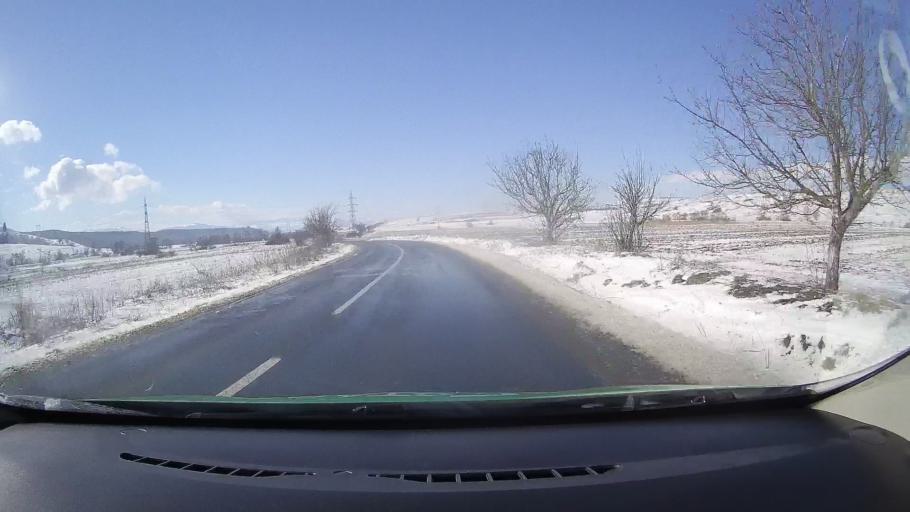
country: RO
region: Sibiu
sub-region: Comuna Rosia
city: Rosia
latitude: 45.7947
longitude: 24.3325
